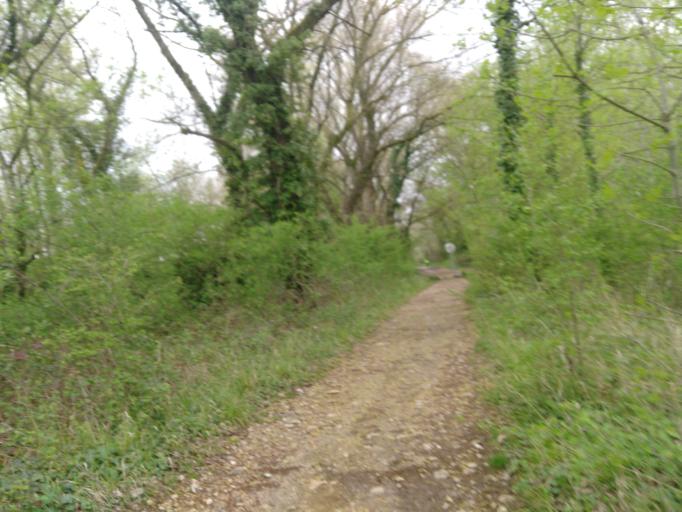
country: FR
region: Rhone-Alpes
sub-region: Departement de la Drome
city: Montboucher-sur-Jabron
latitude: 44.5441
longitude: 4.7888
